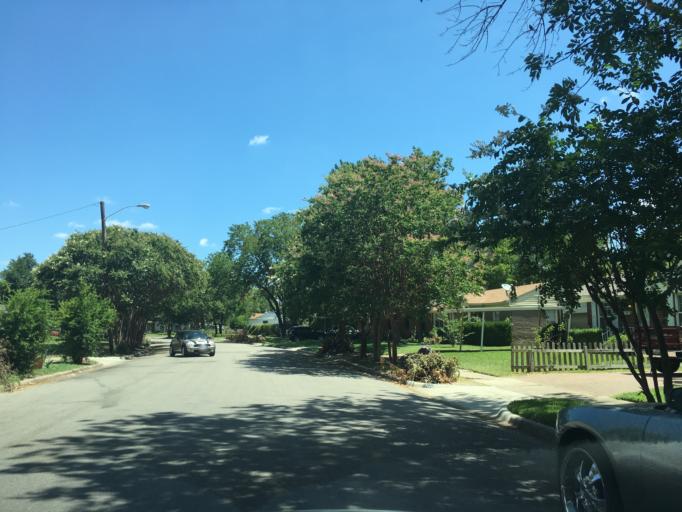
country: US
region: Texas
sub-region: Dallas County
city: Garland
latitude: 32.8400
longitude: -96.6836
